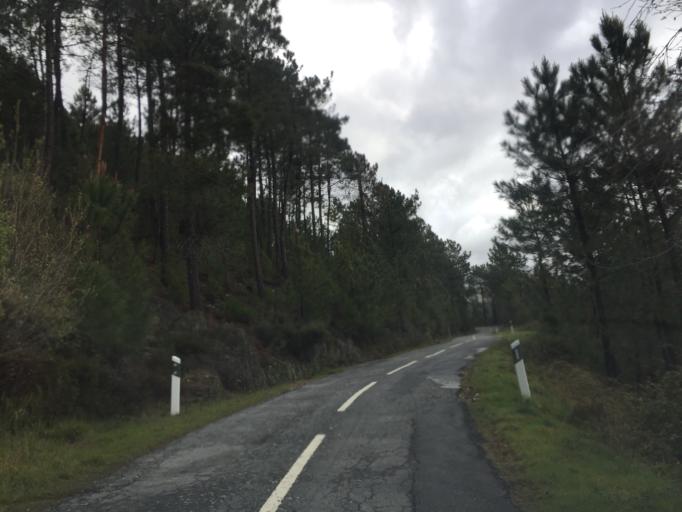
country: PT
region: Guarda
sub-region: Seia
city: Seia
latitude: 40.3224
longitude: -7.7274
